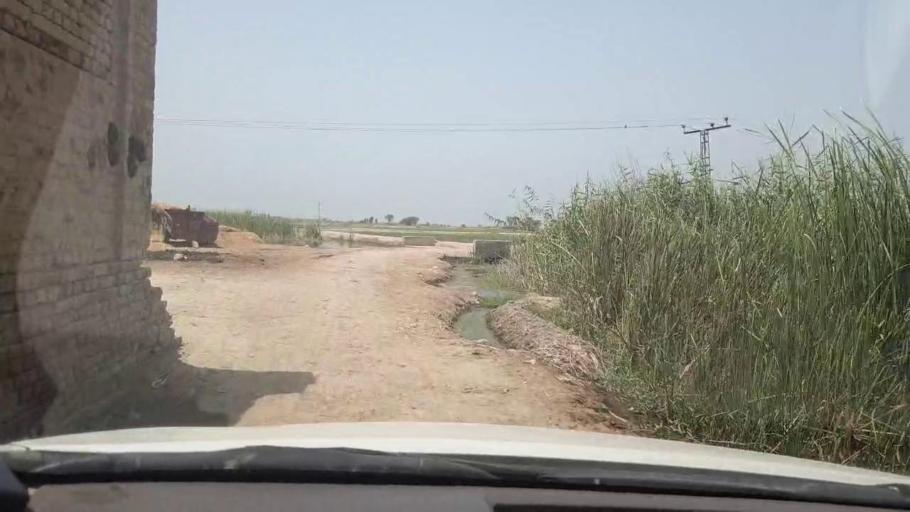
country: PK
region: Sindh
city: Garhi Yasin
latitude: 27.9061
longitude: 68.5474
